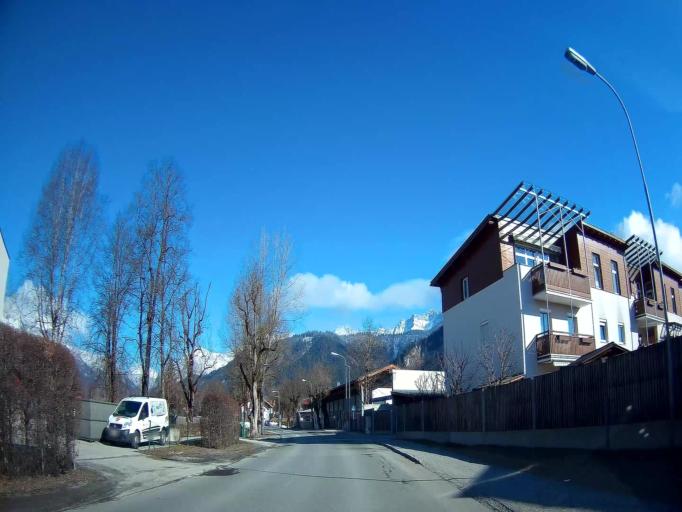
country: AT
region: Salzburg
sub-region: Politischer Bezirk Zell am See
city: Saalfelden am Steinernen Meer
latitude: 47.4305
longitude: 12.8523
